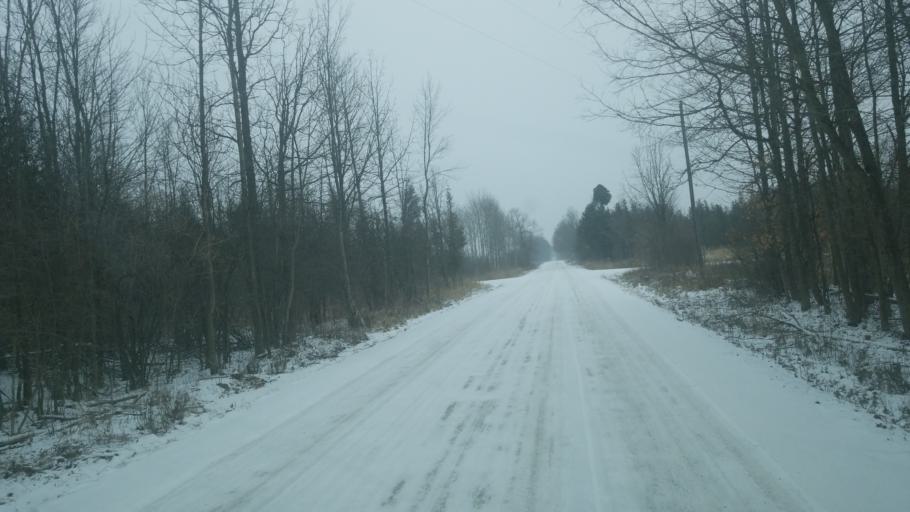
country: US
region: Michigan
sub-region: Osceola County
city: Reed City
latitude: 43.8441
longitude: -85.3940
